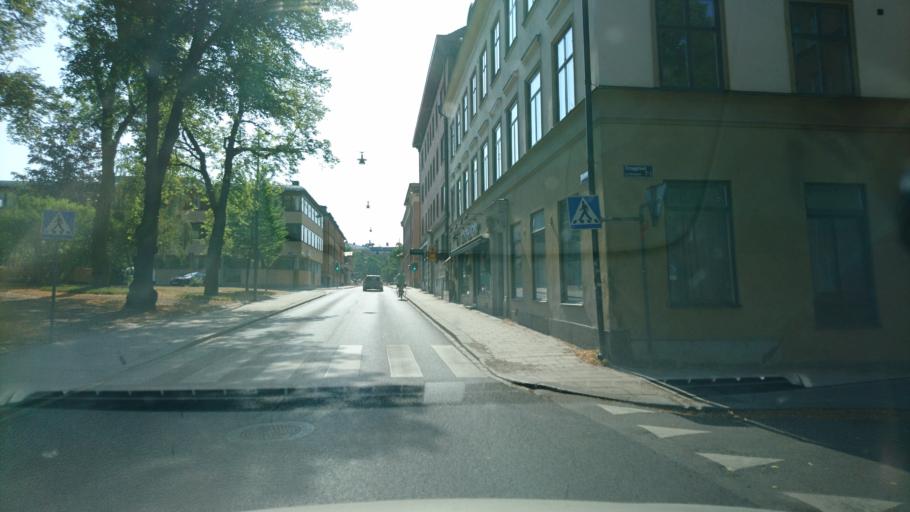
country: SE
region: Uppsala
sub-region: Uppsala Kommun
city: Uppsala
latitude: 59.8570
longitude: 17.6292
